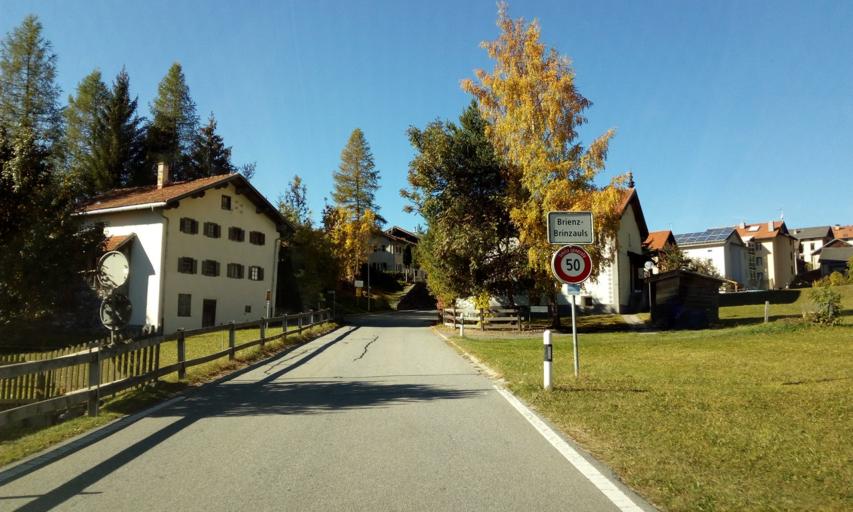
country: CH
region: Grisons
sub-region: Albula District
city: Tiefencastel
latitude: 46.6687
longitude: 9.5983
